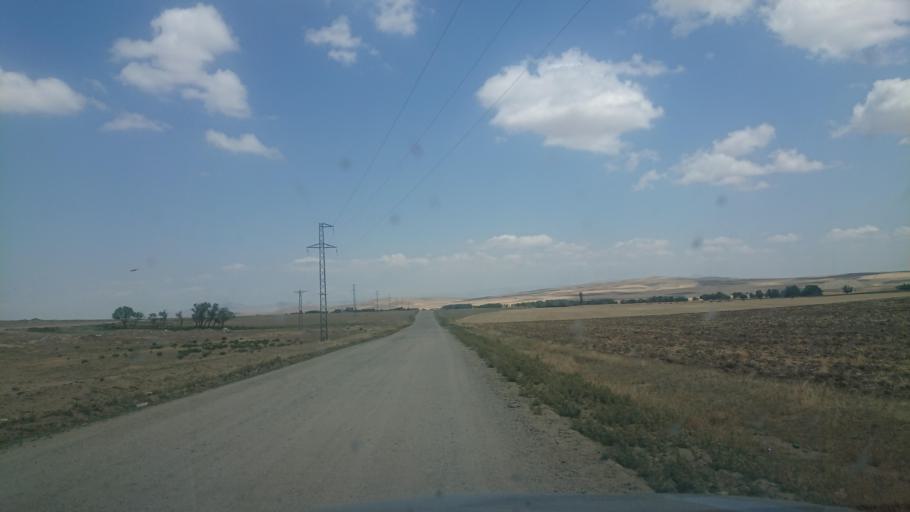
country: TR
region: Aksaray
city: Agacoren
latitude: 38.9376
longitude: 33.9483
